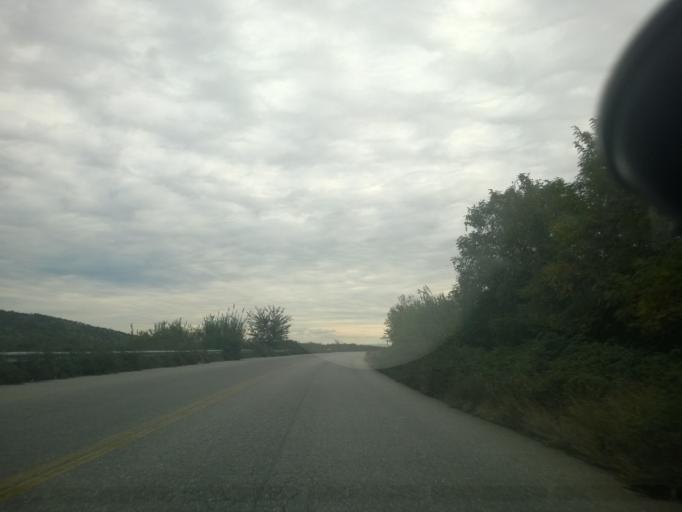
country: GR
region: Central Macedonia
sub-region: Nomos Pellis
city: Profitis Ilias
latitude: 40.8179
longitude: 22.1440
